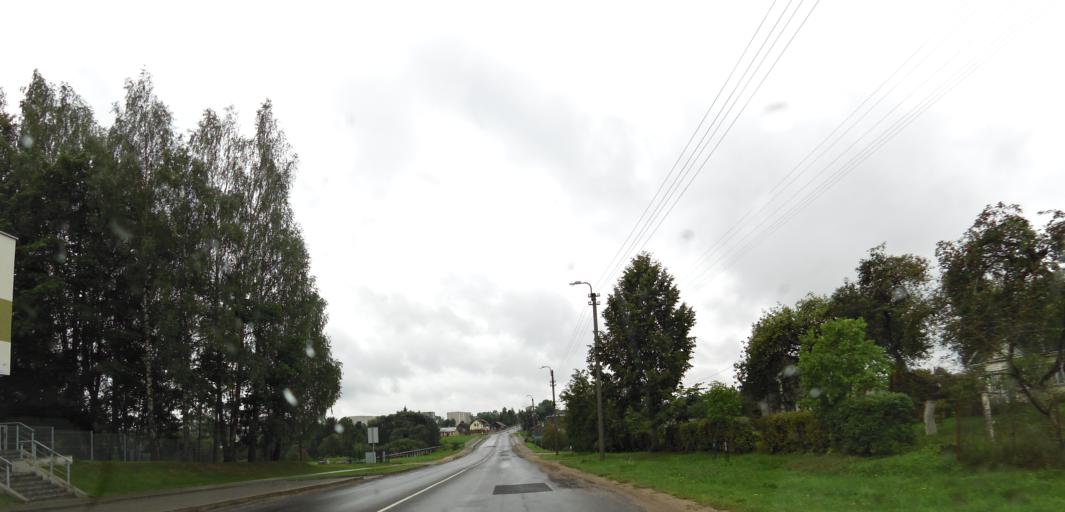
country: LT
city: Sirvintos
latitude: 55.0514
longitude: 24.9478
